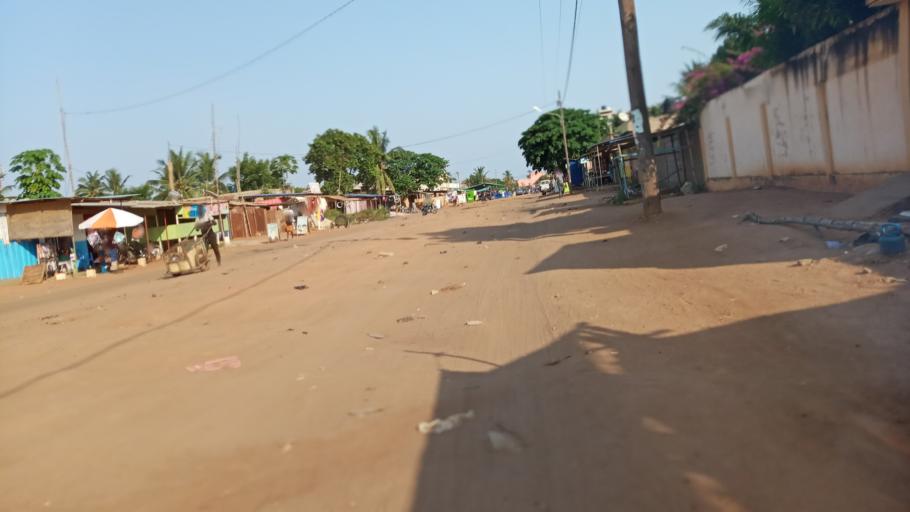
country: TG
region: Maritime
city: Lome
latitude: 6.1811
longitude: 1.1575
